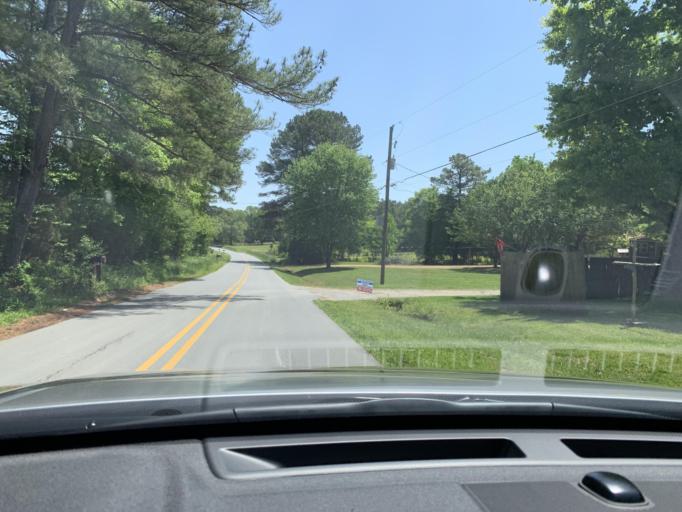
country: US
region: Georgia
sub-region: Polk County
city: Aragon
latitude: 34.0720
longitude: -85.1021
